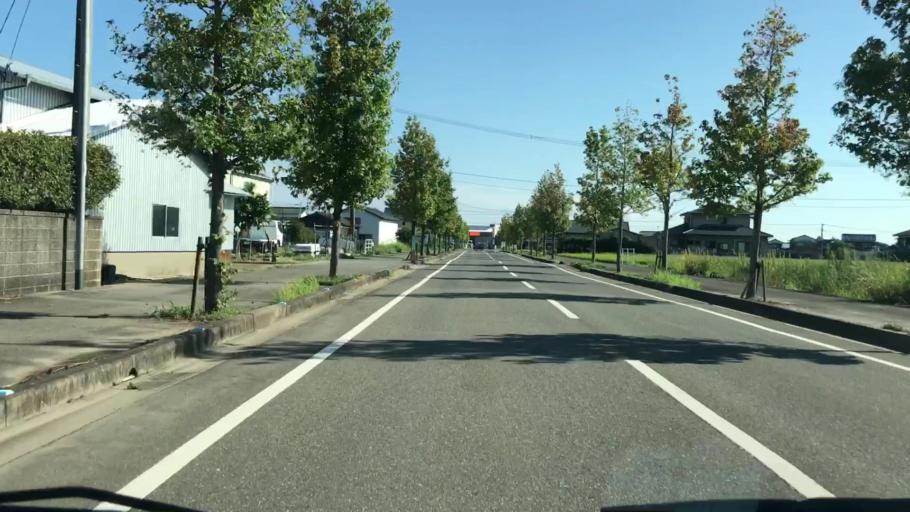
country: JP
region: Saga Prefecture
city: Okawa
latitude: 33.1841
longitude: 130.3138
